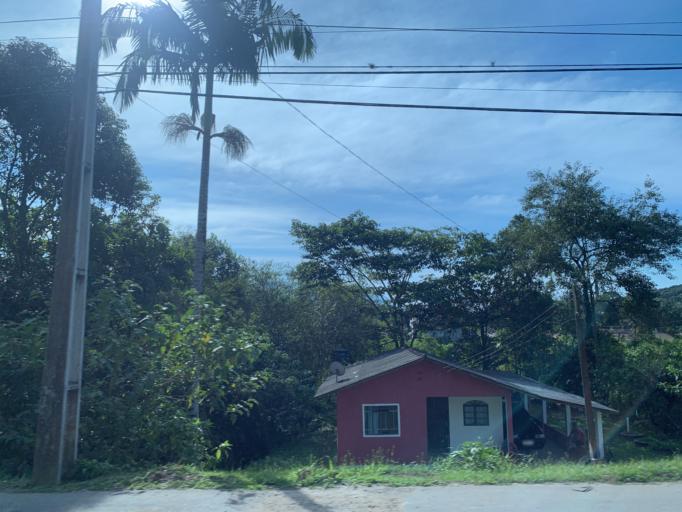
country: BR
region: Parana
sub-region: Antonina
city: Antonina
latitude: -25.4349
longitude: -48.7399
